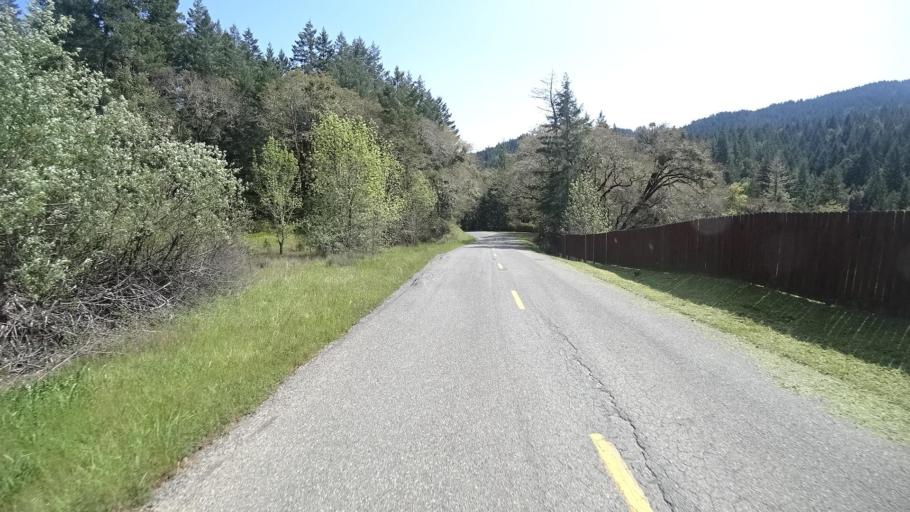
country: US
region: California
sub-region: Humboldt County
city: Redway
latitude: 40.3540
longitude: -123.7189
